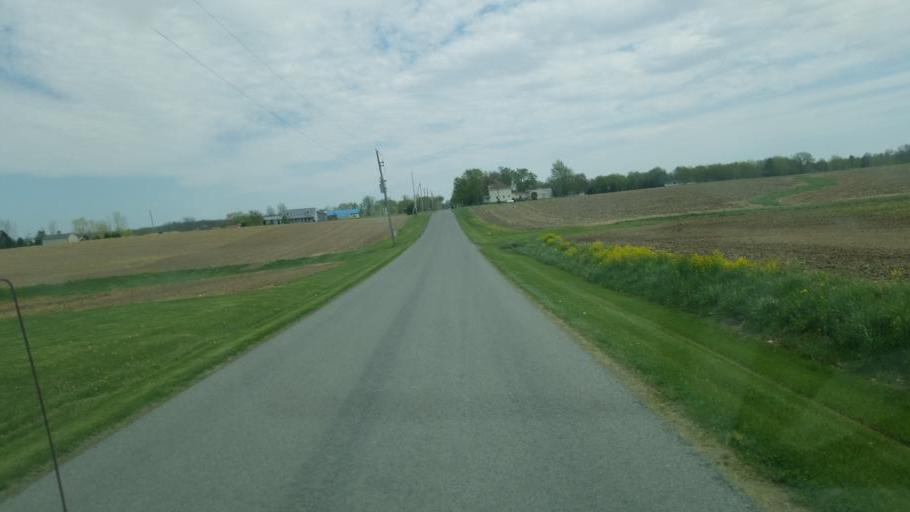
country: US
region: Ohio
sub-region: Allen County
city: Bluffton
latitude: 40.8115
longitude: -83.9651
